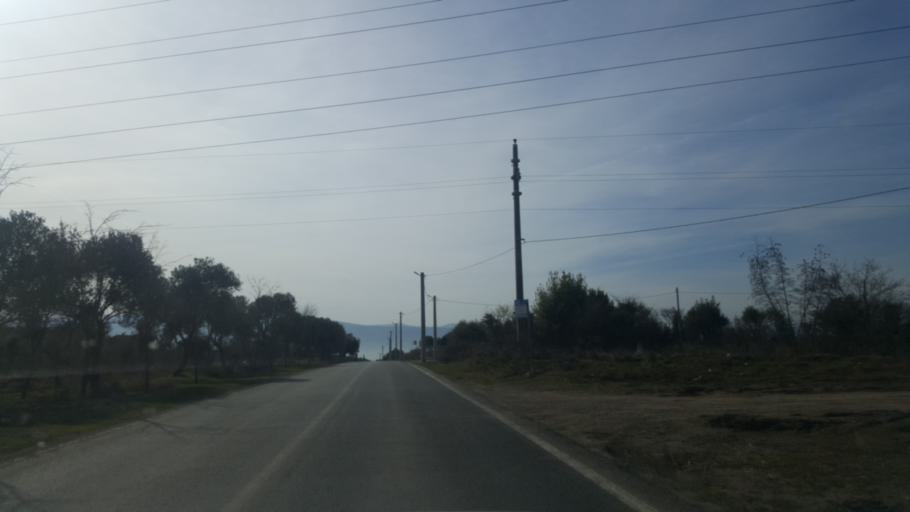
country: TR
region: Kocaeli
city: Tavsancil
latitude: 40.7837
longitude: 29.5737
